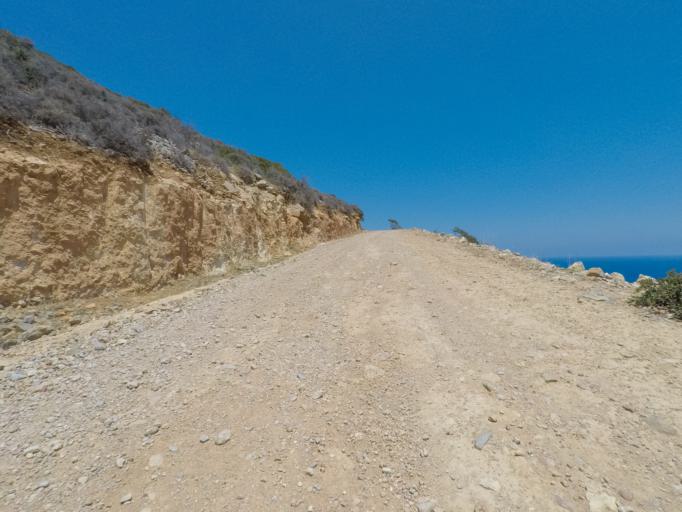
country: GR
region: Crete
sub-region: Nomos Lasithiou
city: Elounda
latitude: 35.3168
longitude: 25.7528
